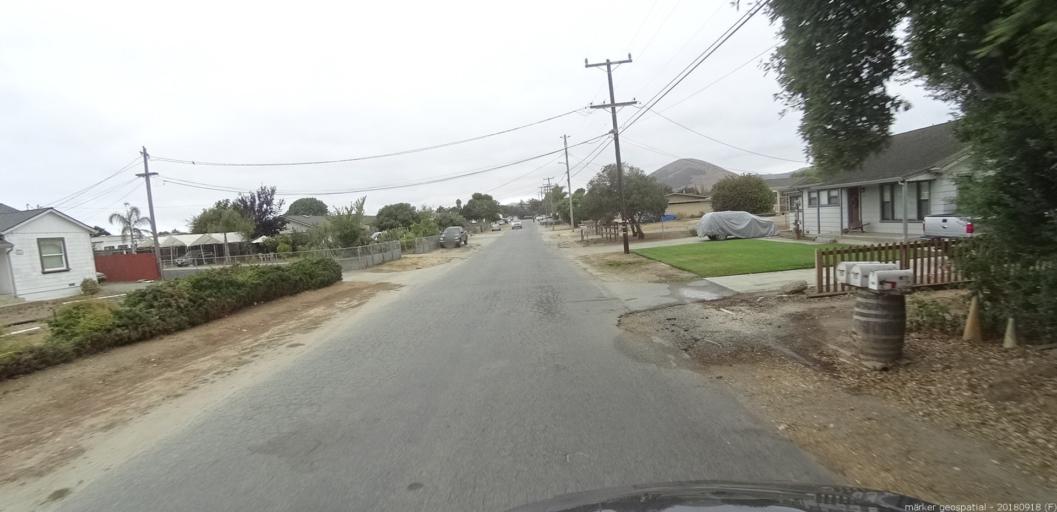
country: US
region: California
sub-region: Monterey County
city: Prunedale
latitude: 36.7556
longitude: -121.6160
